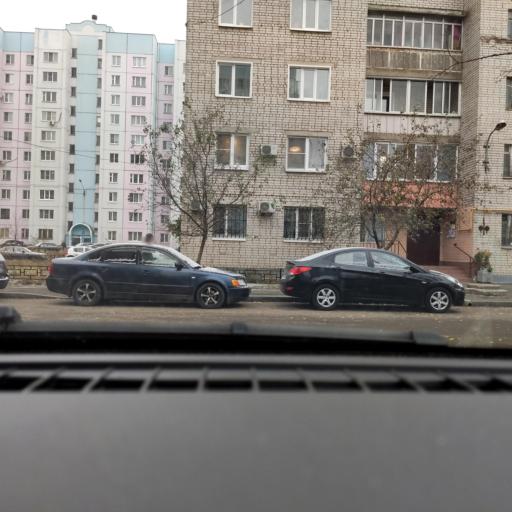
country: RU
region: Voronezj
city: Somovo
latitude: 51.7353
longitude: 39.2947
